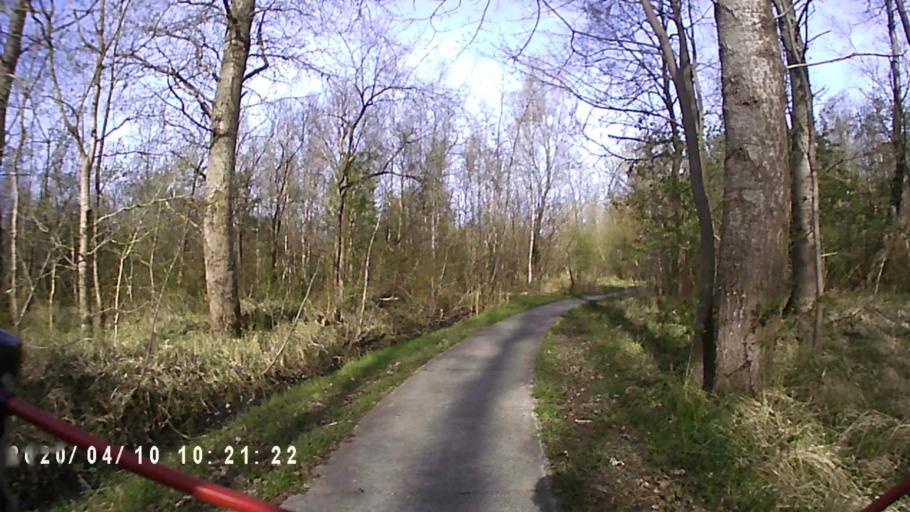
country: NL
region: Friesland
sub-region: Gemeente Dongeradeel
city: Anjum
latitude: 53.3808
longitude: 6.2181
